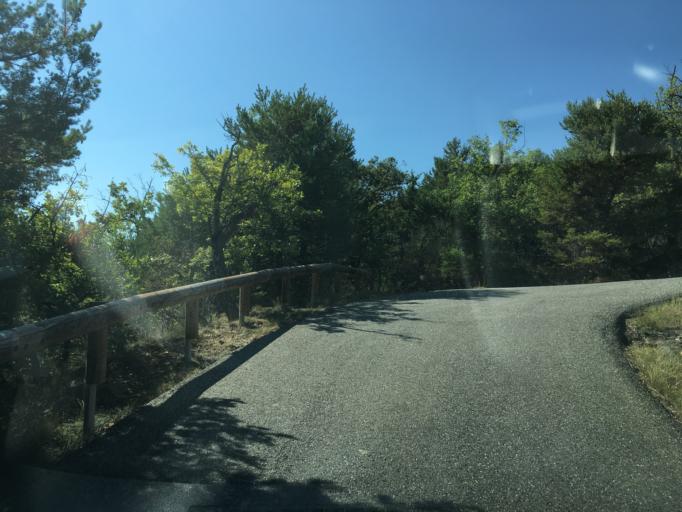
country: FR
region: Provence-Alpes-Cote d'Azur
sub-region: Departement des Alpes-de-Haute-Provence
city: Mallemoisson
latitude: 44.0667
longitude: 6.1314
